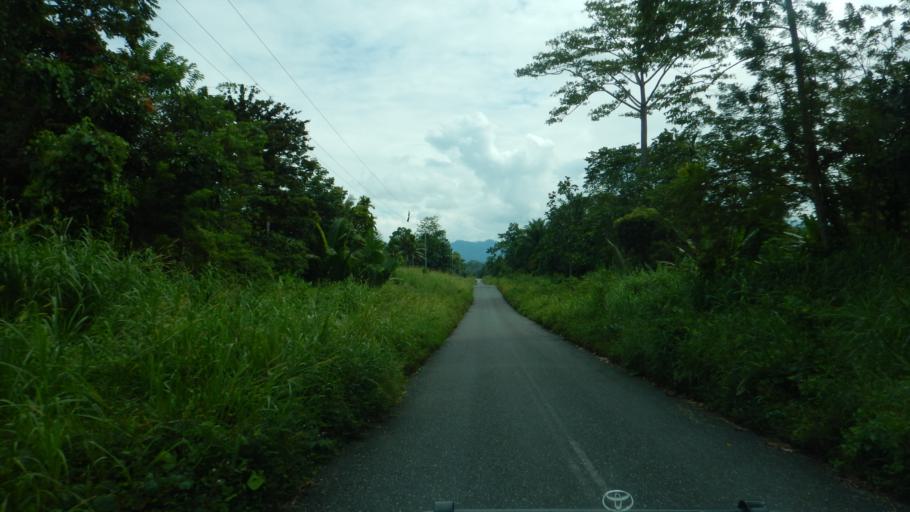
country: PG
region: Northern Province
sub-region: Sohe
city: Popondetta
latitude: -8.8521
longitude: 148.0232
